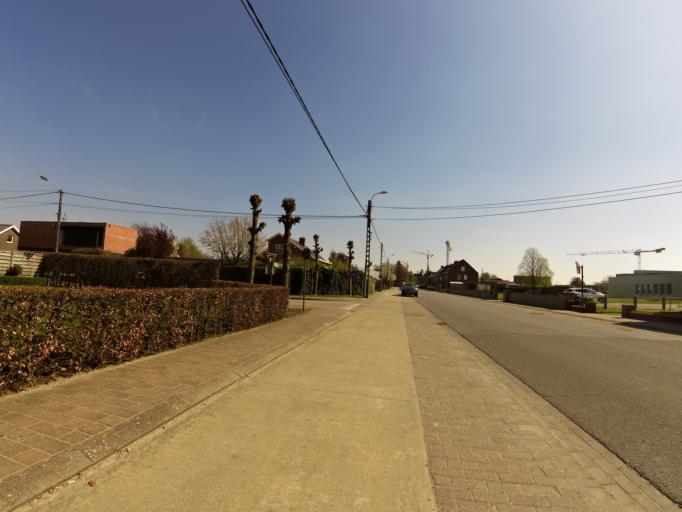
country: BE
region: Flanders
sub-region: Provincie West-Vlaanderen
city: Kortemark
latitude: 51.0336
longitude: 3.0397
